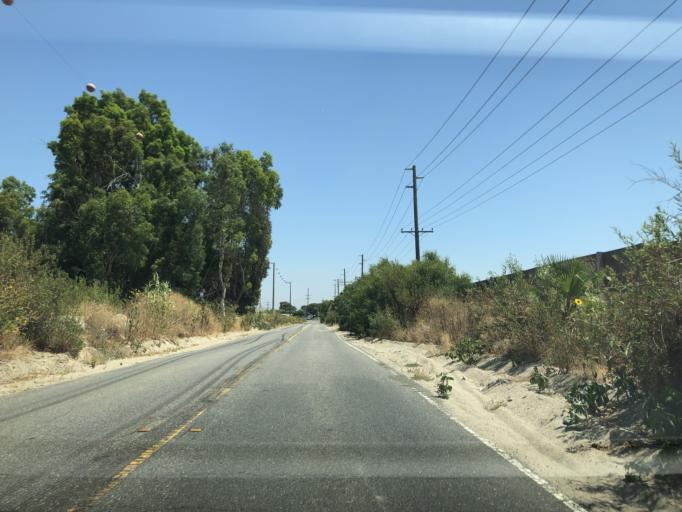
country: US
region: California
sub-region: Riverside County
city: Corona
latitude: 33.8987
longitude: -117.5925
